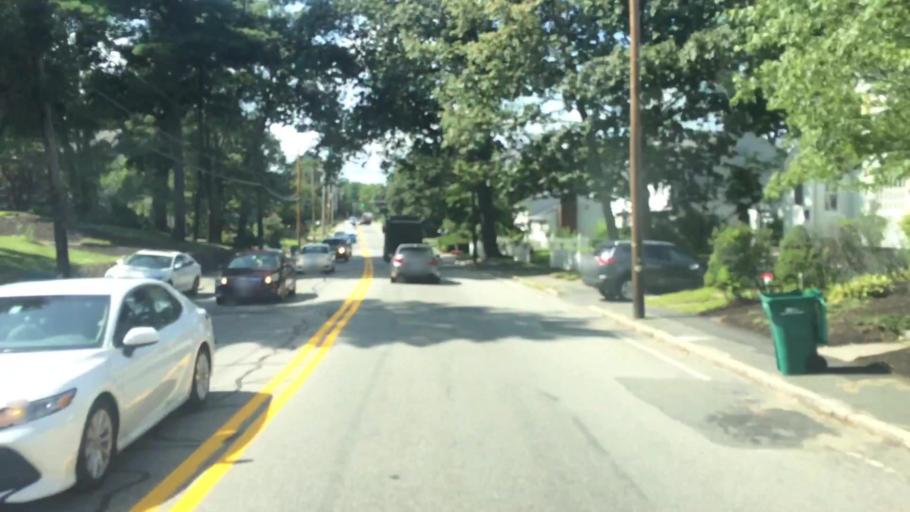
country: US
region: Massachusetts
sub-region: Essex County
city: South Peabody
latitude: 42.5085
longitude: -70.9865
